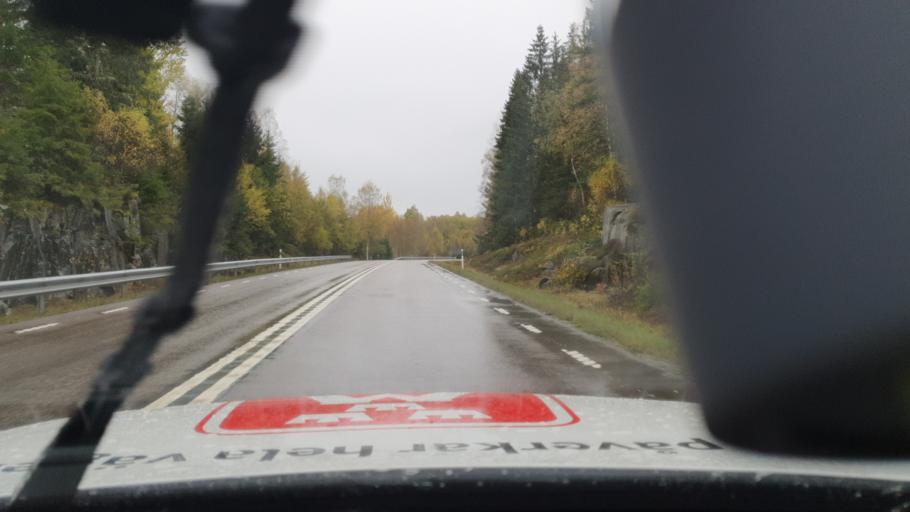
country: SE
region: Vaestra Goetaland
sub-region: Dals-Ed Kommun
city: Ed
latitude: 58.9333
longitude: 12.0589
